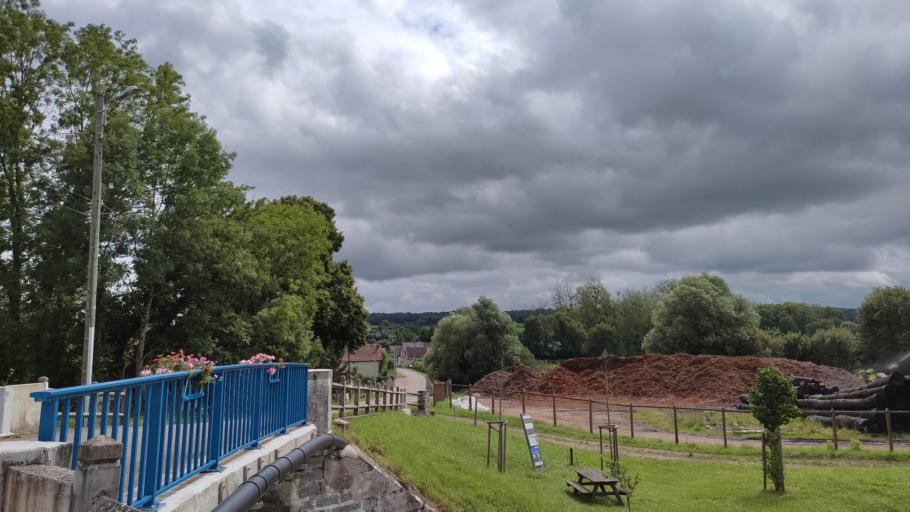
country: FR
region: Bourgogne
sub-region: Departement de la Nievre
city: Corbigny
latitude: 47.3287
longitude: 3.6548
